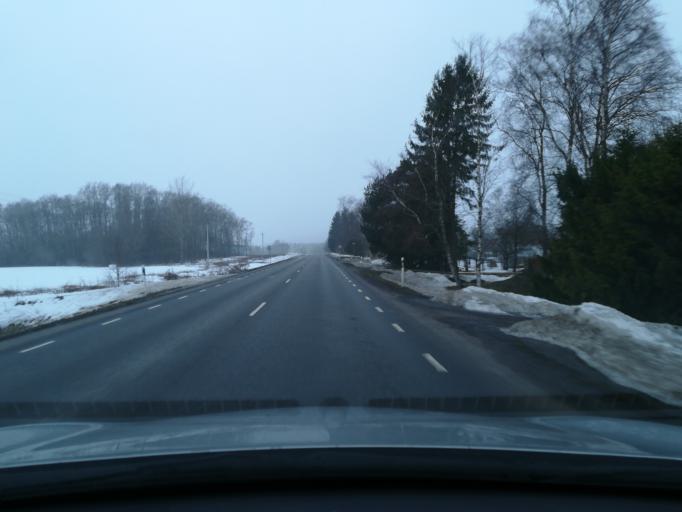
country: EE
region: Harju
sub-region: Raasiku vald
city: Raasiku
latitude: 59.3629
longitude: 25.1785
